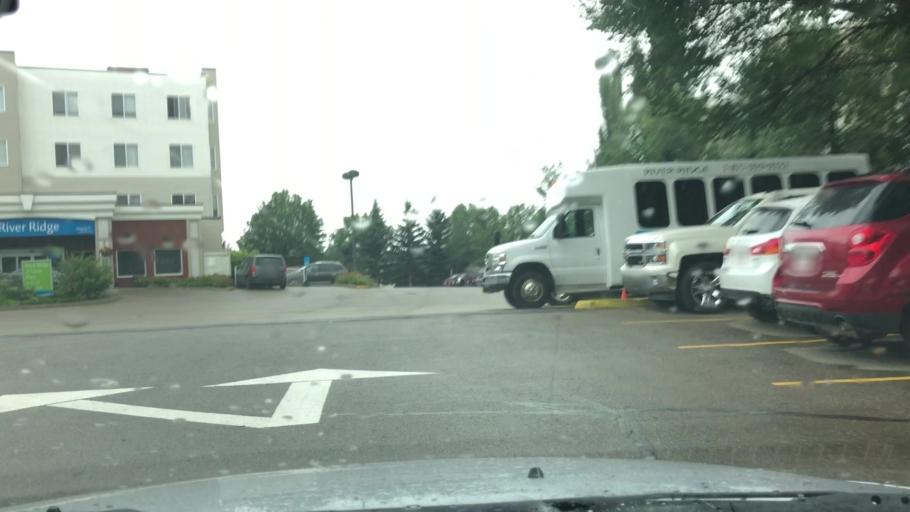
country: CA
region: Alberta
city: St. Albert
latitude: 53.6400
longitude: -113.6350
